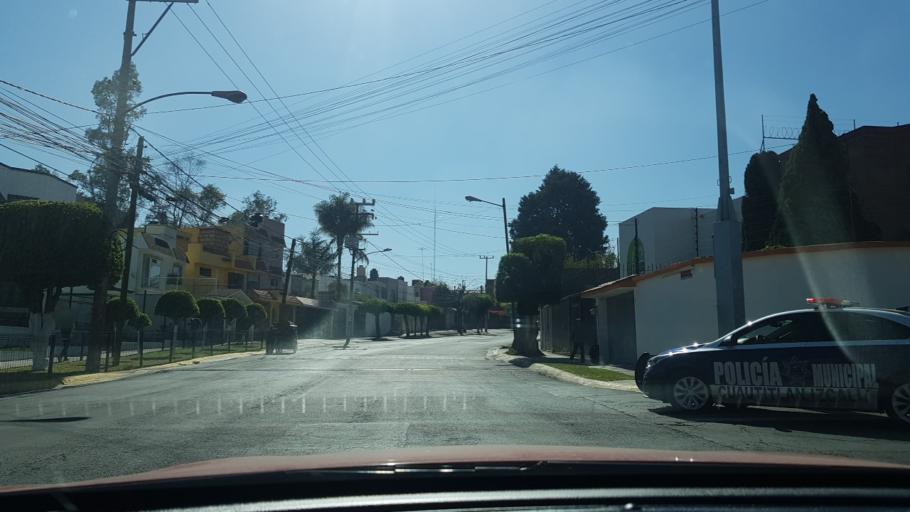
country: MX
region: Mexico
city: Cuautitlan Izcalli
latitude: 19.6470
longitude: -99.2007
